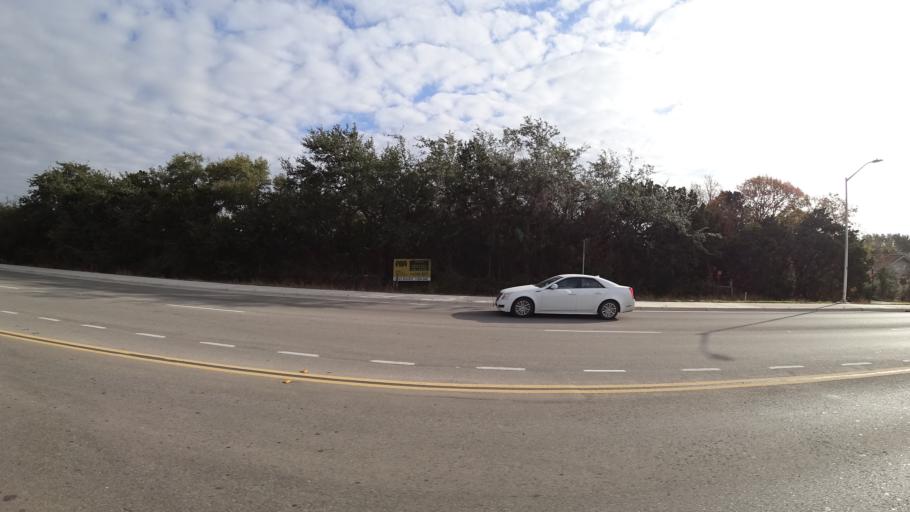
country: US
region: Texas
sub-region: Williamson County
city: Cedar Park
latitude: 30.5232
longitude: -97.8425
